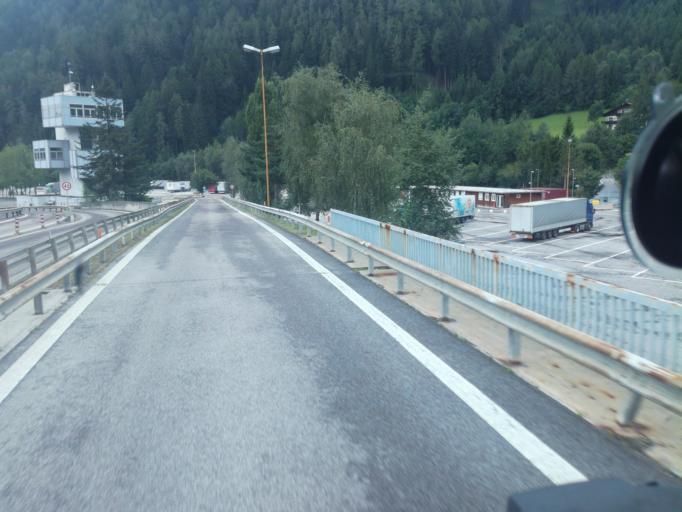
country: IT
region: Trentino-Alto Adige
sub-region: Bolzano
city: Vipiteno
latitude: 46.8834
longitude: 11.4333
